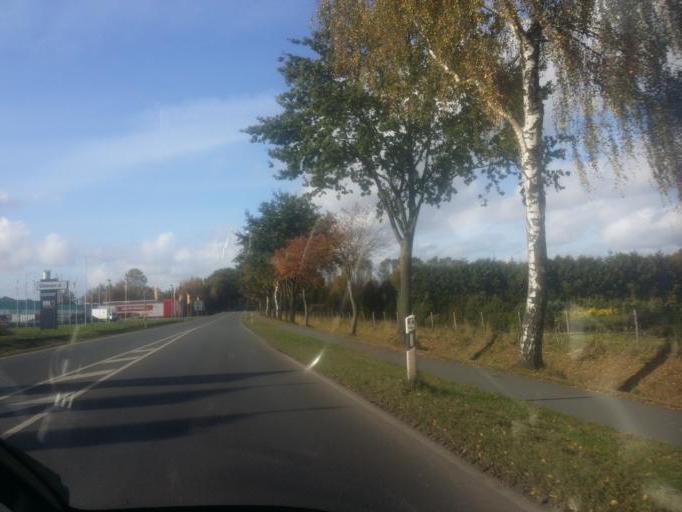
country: DE
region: Schleswig-Holstein
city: Elmshorn
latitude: 53.7762
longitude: 9.6610
